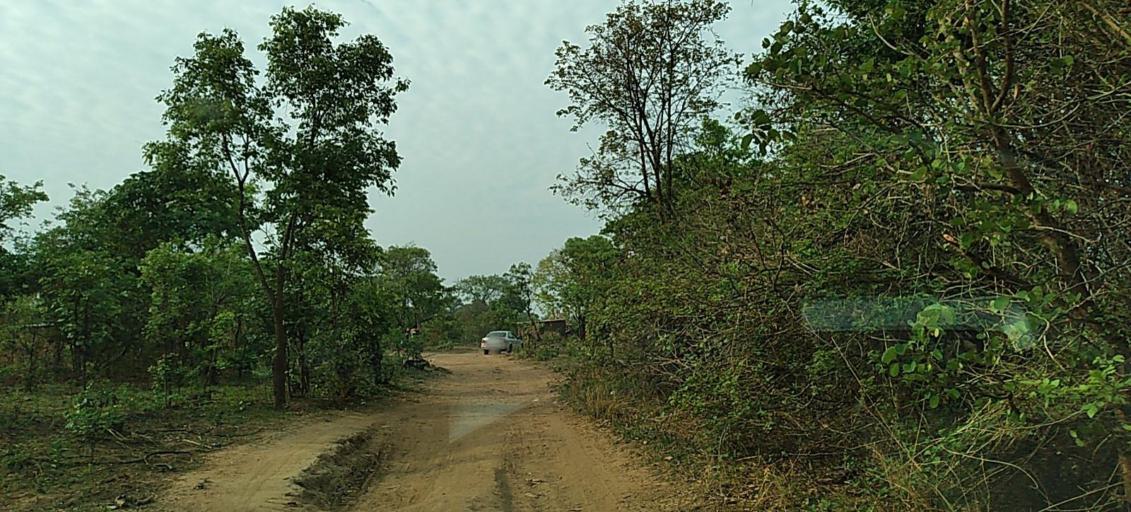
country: ZM
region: Copperbelt
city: Kalulushi
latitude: -12.9147
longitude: 27.6880
